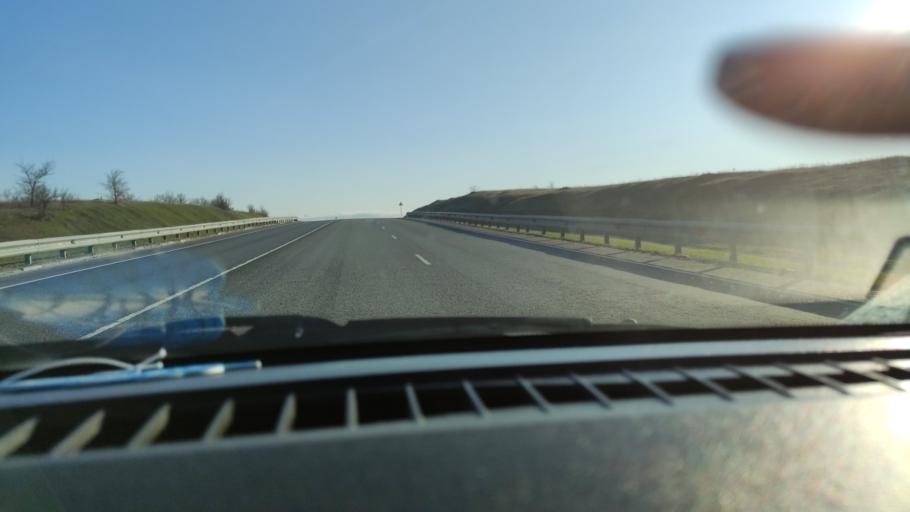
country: RU
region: Saratov
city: Alekseyevka
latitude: 52.2204
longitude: 47.8966
